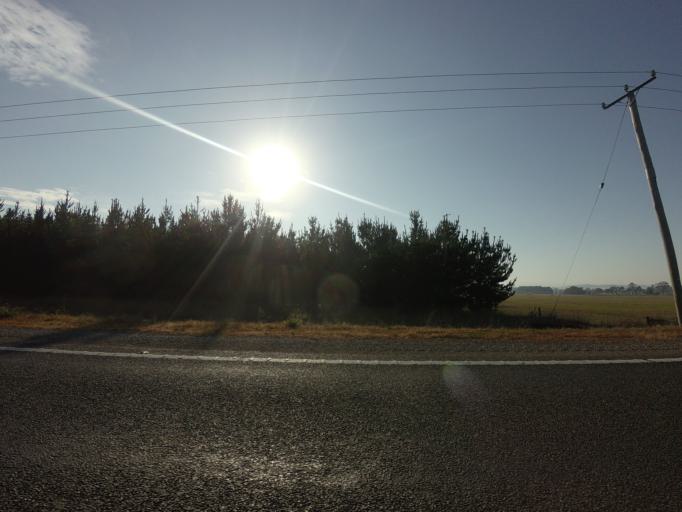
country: AU
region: Tasmania
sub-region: Northern Midlands
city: Longford
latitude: -41.5448
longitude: 147.0570
